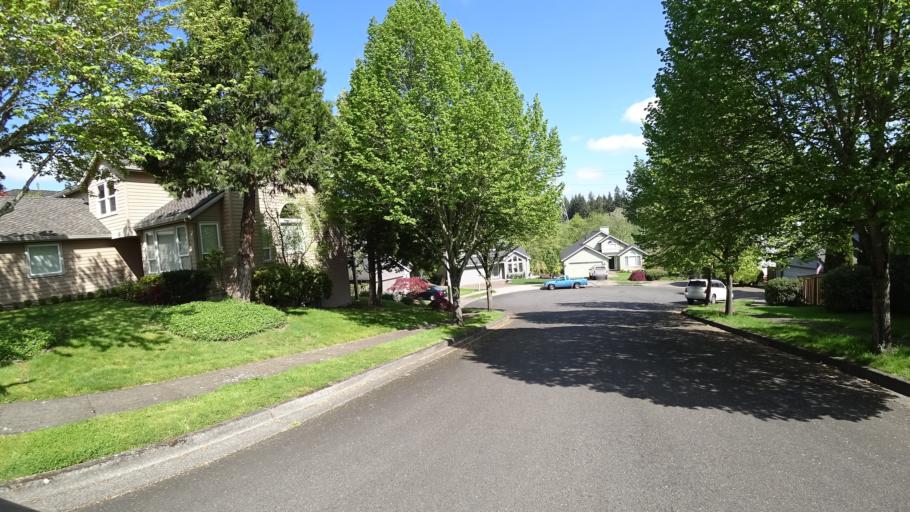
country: US
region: Oregon
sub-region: Washington County
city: King City
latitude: 45.4389
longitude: -122.8345
